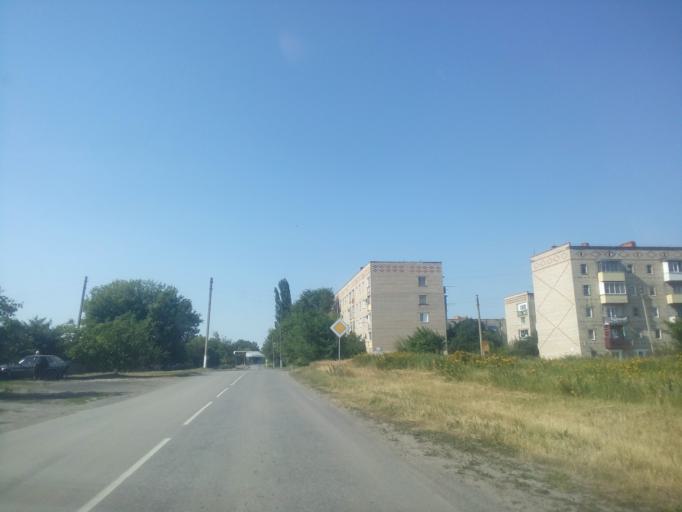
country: RU
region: Rostov
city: Sholokhovskiy
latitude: 48.2750
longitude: 41.0370
